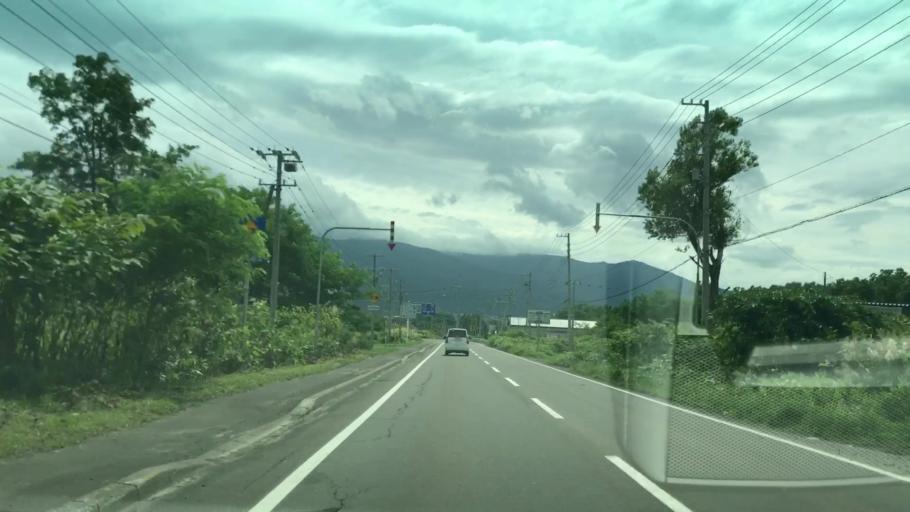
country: JP
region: Hokkaido
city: Iwanai
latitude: 43.0003
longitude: 140.5397
